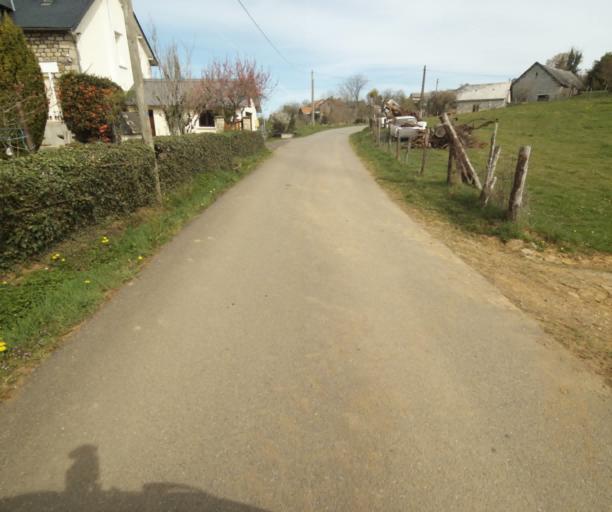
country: FR
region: Limousin
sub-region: Departement de la Correze
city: Correze
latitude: 45.3579
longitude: 1.8149
